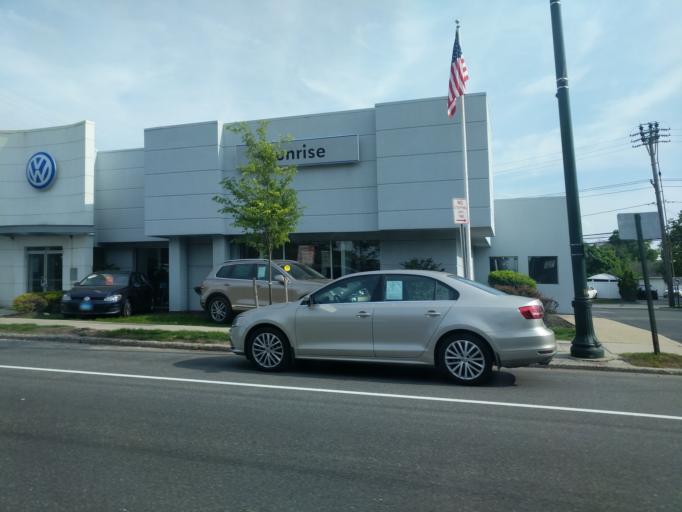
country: US
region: New York
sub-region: Nassau County
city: Hewlett
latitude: 40.6573
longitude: -73.6883
